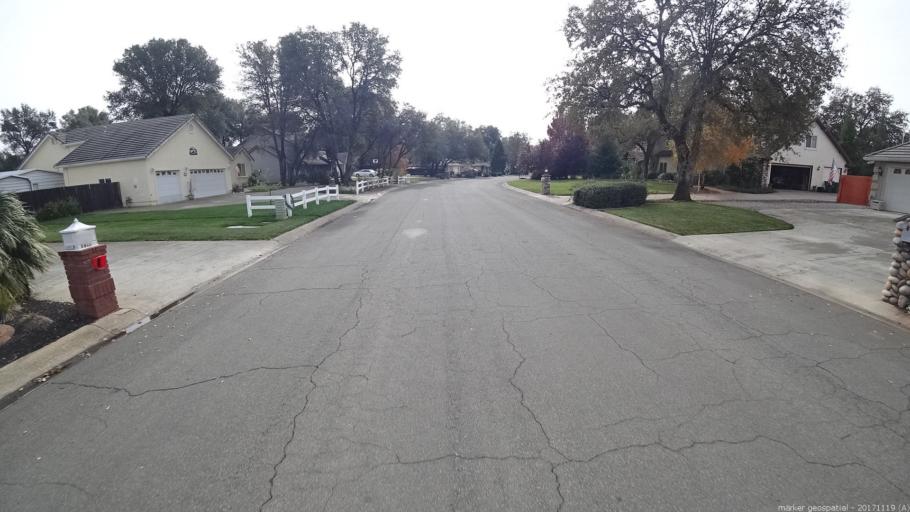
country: US
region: California
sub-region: Shasta County
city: Anderson
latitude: 40.4835
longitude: -122.2966
